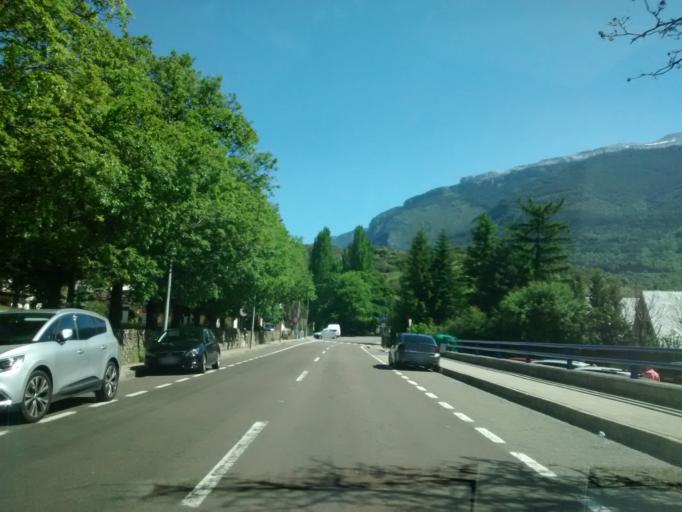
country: ES
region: Aragon
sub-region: Provincia de Huesca
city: Villanua
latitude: 42.6812
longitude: -0.5361
